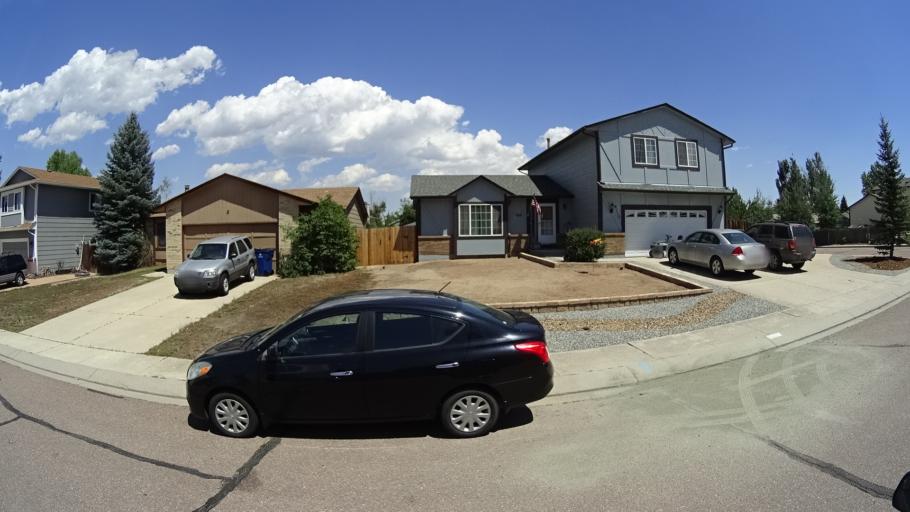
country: US
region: Colorado
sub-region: El Paso County
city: Black Forest
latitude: 38.9495
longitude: -104.7478
